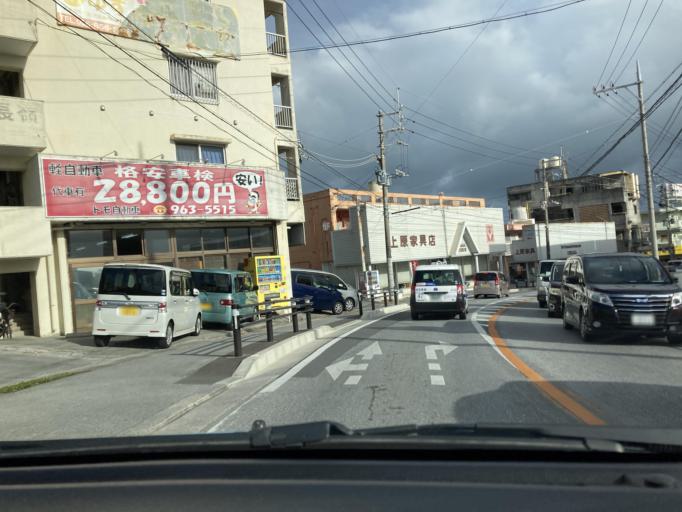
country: JP
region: Okinawa
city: Tomigusuku
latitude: 26.1800
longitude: 127.6643
